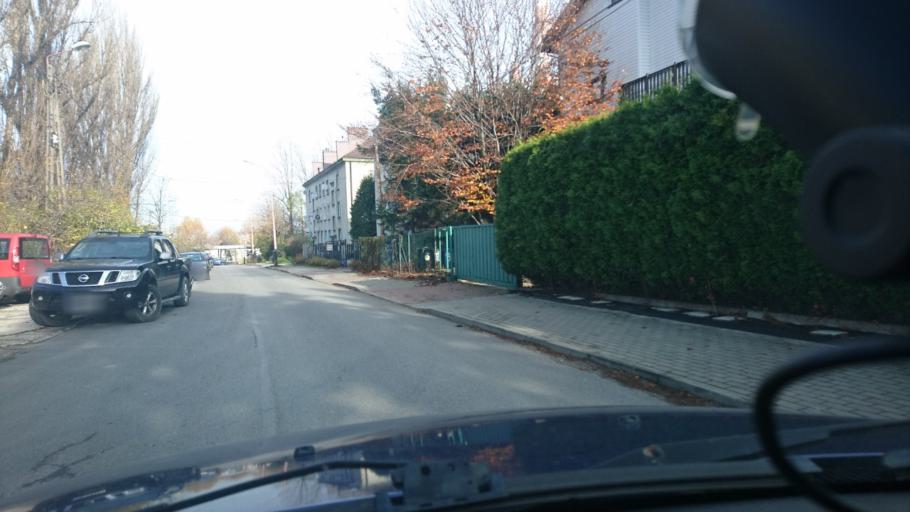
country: PL
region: Silesian Voivodeship
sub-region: Bielsko-Biala
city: Bielsko-Biala
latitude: 49.8090
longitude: 19.0517
